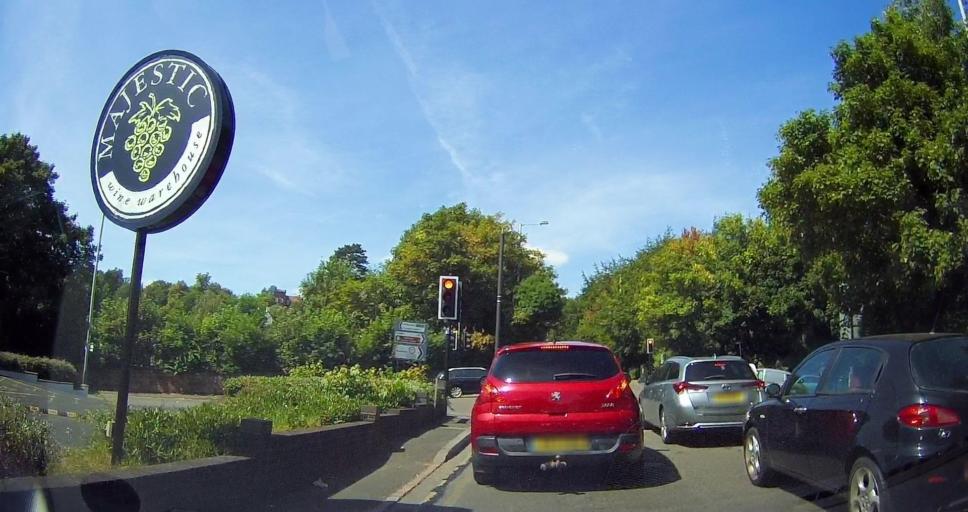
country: GB
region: England
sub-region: Wolverhampton
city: Wolverhampton
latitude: 52.5977
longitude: -2.1614
